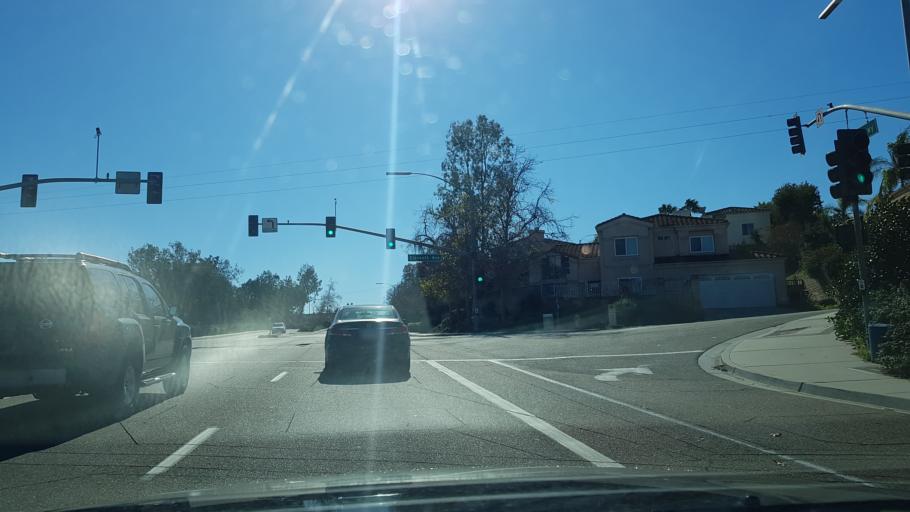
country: US
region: California
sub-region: San Diego County
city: Escondido
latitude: 33.1075
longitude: -117.1046
